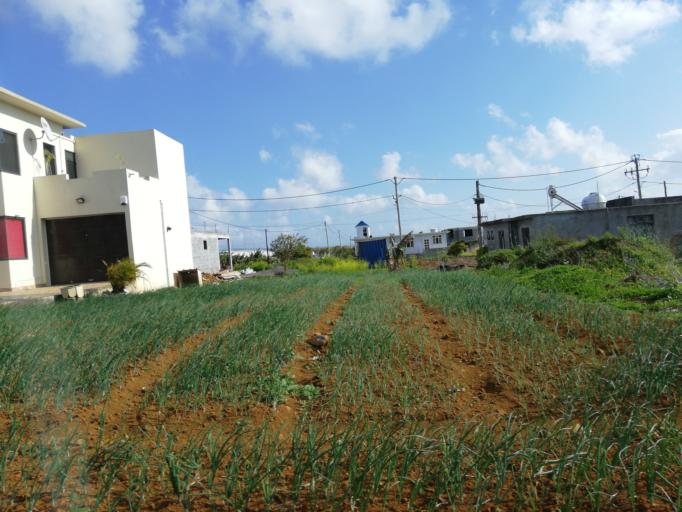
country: MU
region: Moka
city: Verdun
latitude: -20.2247
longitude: 57.5466
